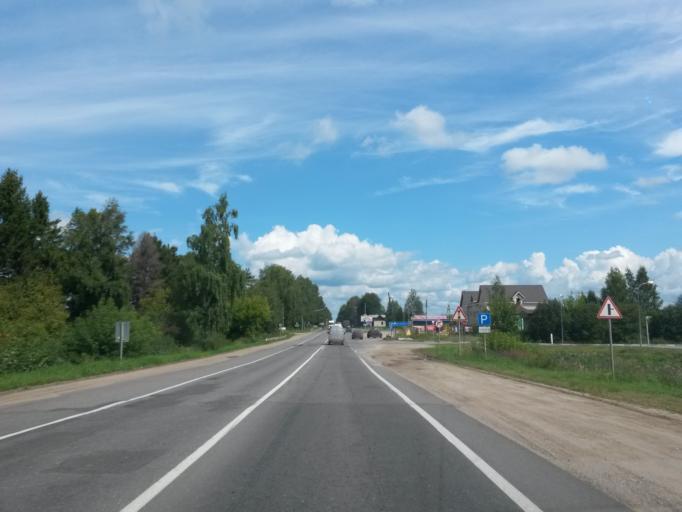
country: RU
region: Jaroslavl
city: Pereslavl'-Zalesskiy
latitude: 56.7801
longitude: 38.8811
